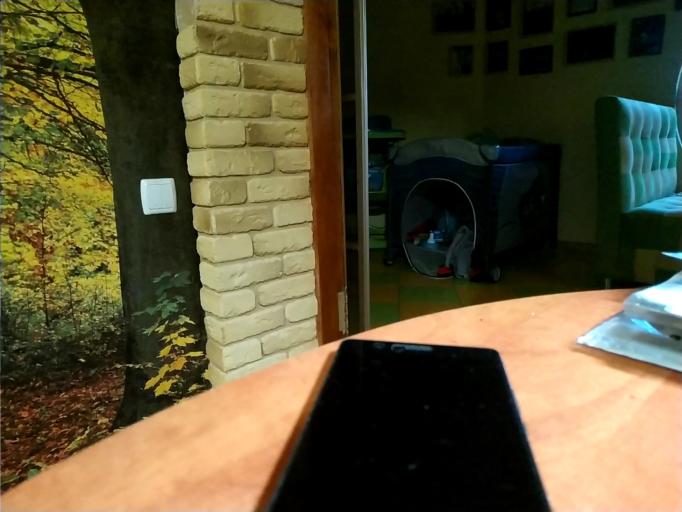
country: RU
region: Orjol
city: Znamenskoye
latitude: 53.4218
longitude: 35.5371
